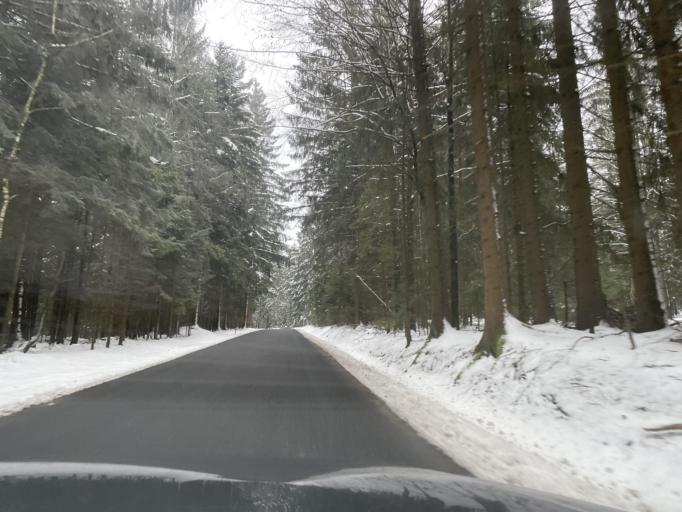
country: DE
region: Bavaria
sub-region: Lower Bavaria
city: Viechtach
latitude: 49.1367
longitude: 12.9100
